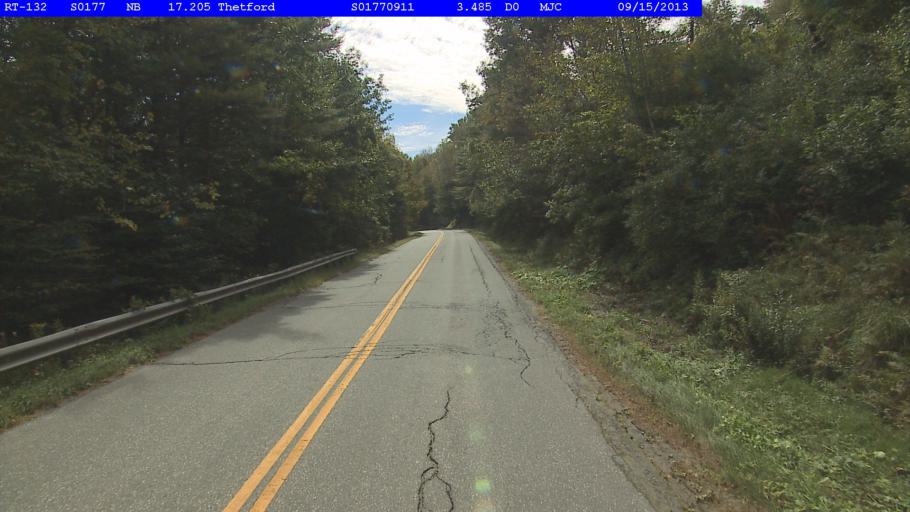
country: US
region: New Hampshire
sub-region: Grafton County
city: Hanover
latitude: 43.8085
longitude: -72.2718
